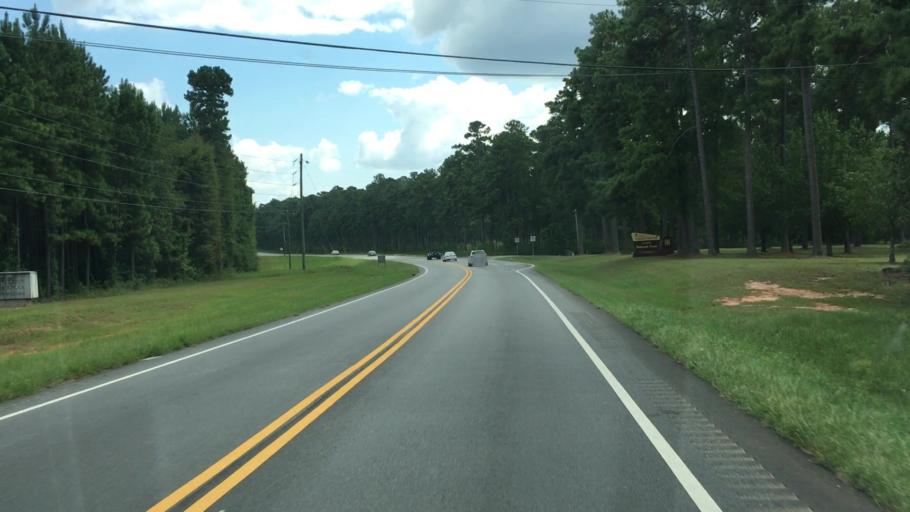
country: US
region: Georgia
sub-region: Putnam County
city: Jefferson
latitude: 33.4143
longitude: -83.3722
